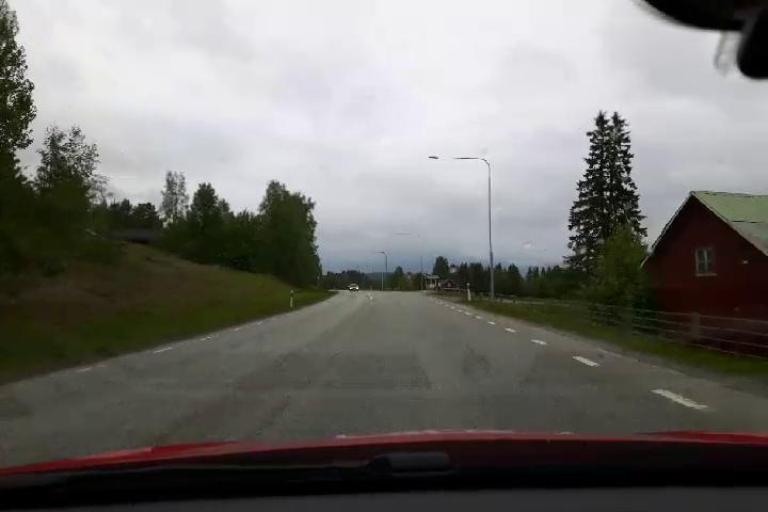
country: SE
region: Jaemtland
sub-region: Bergs Kommun
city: Hoverberg
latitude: 62.6598
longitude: 14.3808
